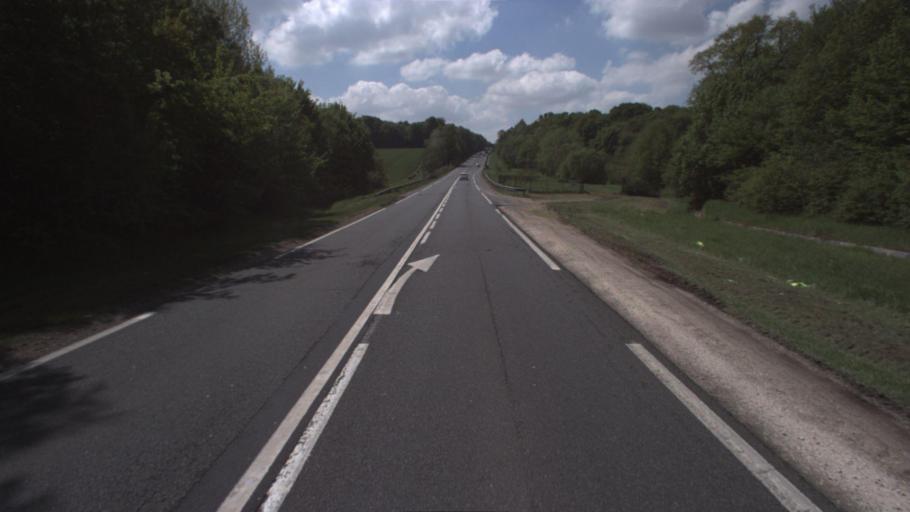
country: FR
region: Ile-de-France
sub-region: Departement de Seine-et-Marne
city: Guignes
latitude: 48.6598
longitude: 2.8087
